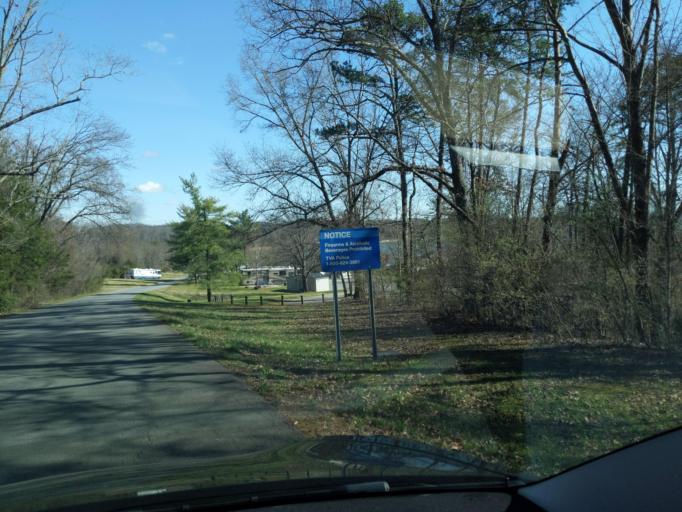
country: US
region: Tennessee
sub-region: Sevier County
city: Sevierville
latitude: 35.9558
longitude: -83.5373
